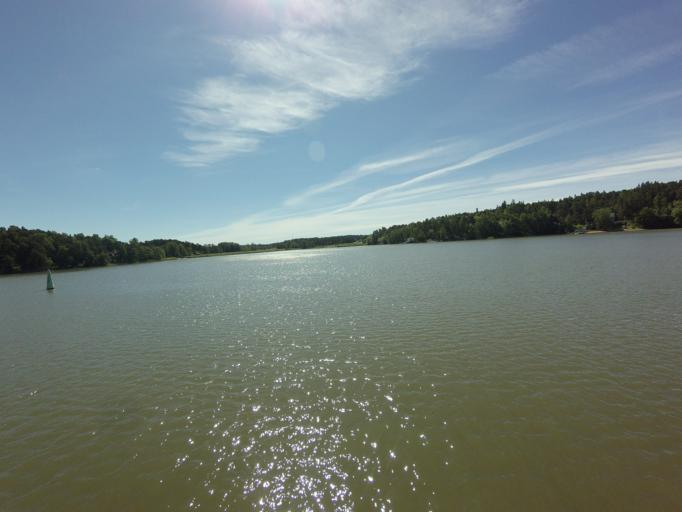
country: FI
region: Varsinais-Suomi
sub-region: Turku
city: Raisio
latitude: 60.4210
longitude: 22.1714
